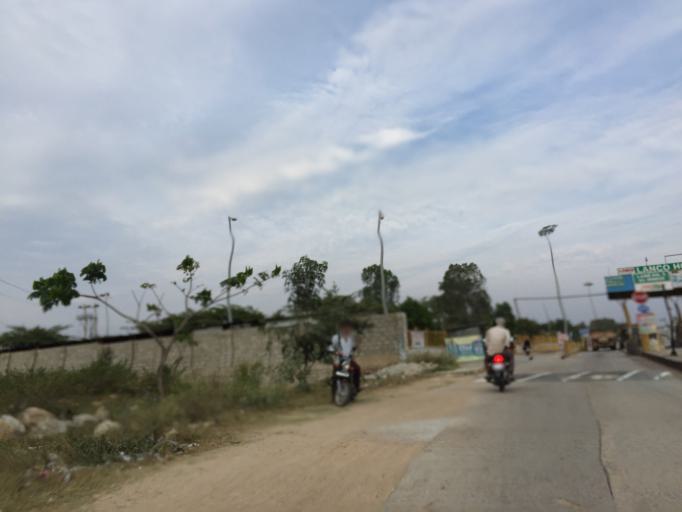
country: IN
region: Karnataka
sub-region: Kolar
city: Mulbagal
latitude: 13.1485
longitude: 78.2898
